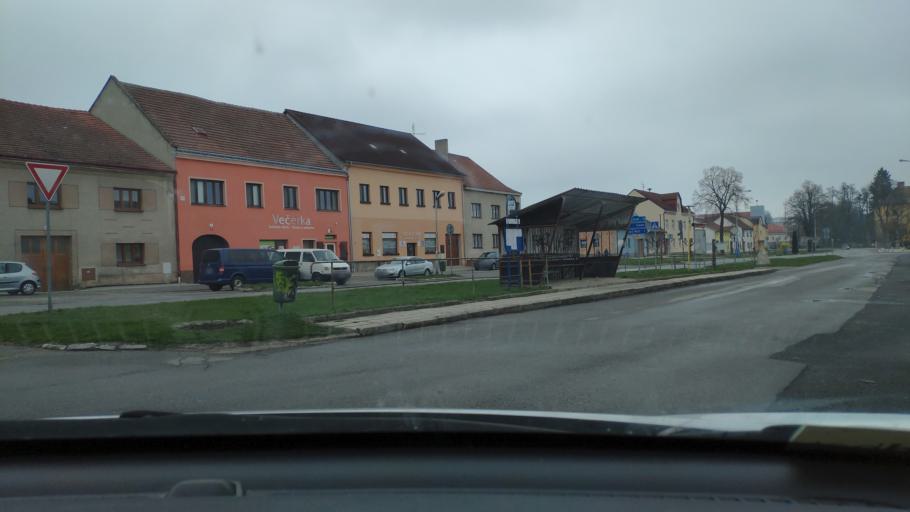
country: CZ
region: Vysocina
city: Batelov
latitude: 49.3134
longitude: 15.3948
